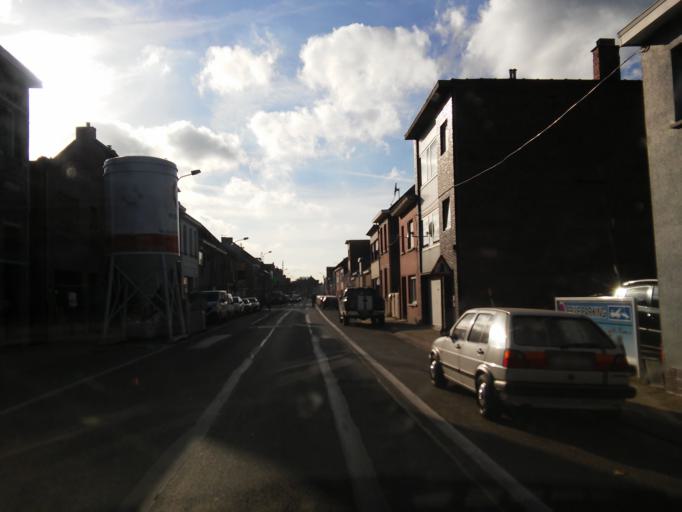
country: BE
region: Flanders
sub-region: Provincie Antwerpen
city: Berlaar
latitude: 51.1153
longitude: 4.6456
